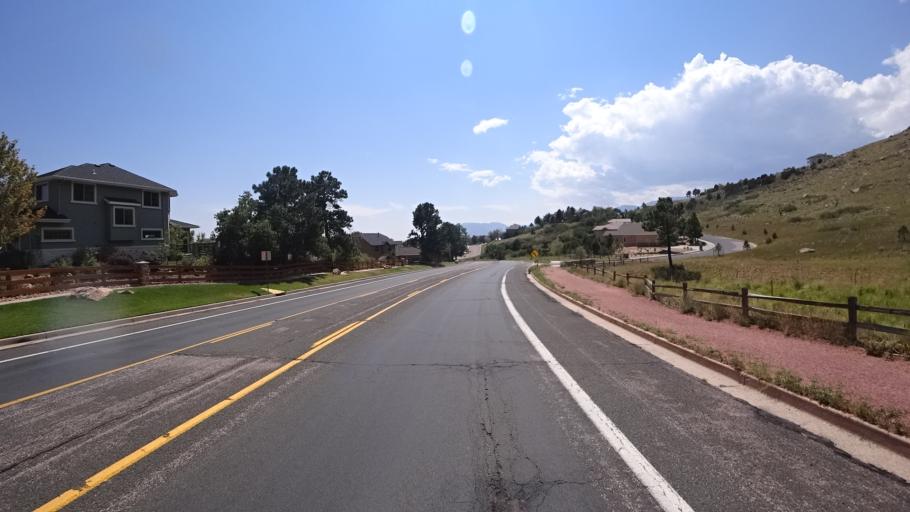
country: US
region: Colorado
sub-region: El Paso County
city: Manitou Springs
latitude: 38.9126
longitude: -104.8754
